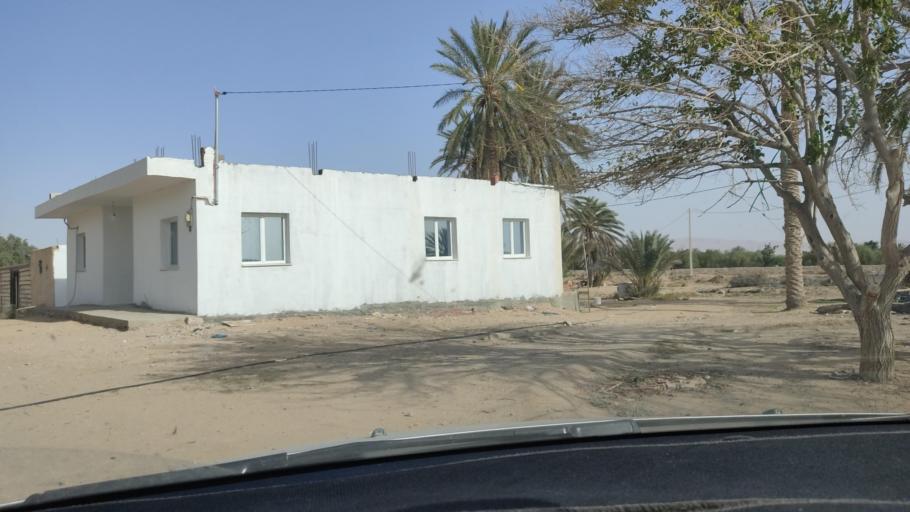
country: TN
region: Gafsa
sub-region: Gafsa Municipality
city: Gafsa
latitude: 34.3515
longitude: 8.8626
